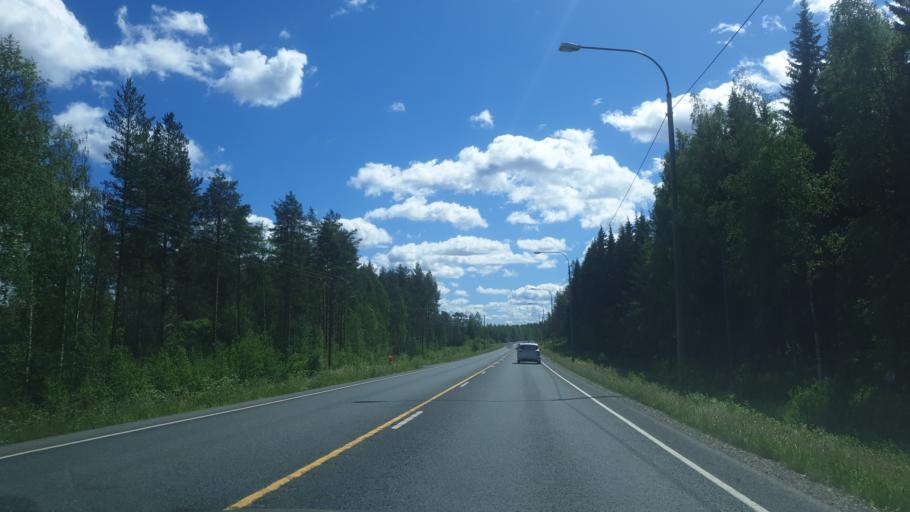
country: FI
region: Northern Savo
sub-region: Varkaus
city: Leppaevirta
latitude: 62.5362
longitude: 27.6460
